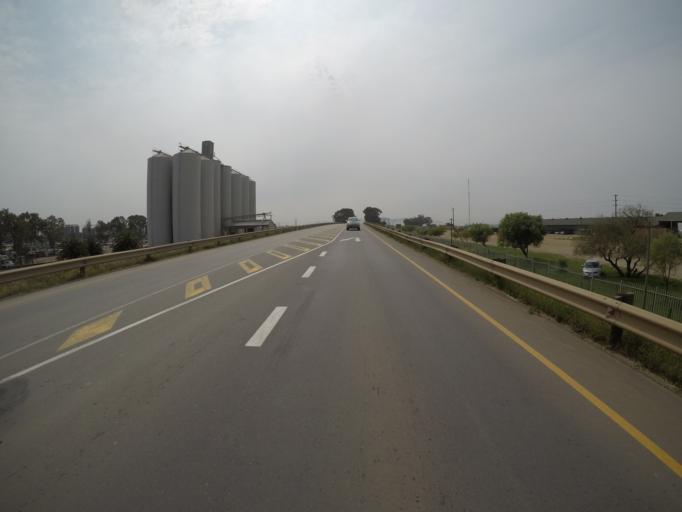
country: ZA
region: Western Cape
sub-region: City of Cape Town
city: Kraaifontein
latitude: -33.7044
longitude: 18.7012
